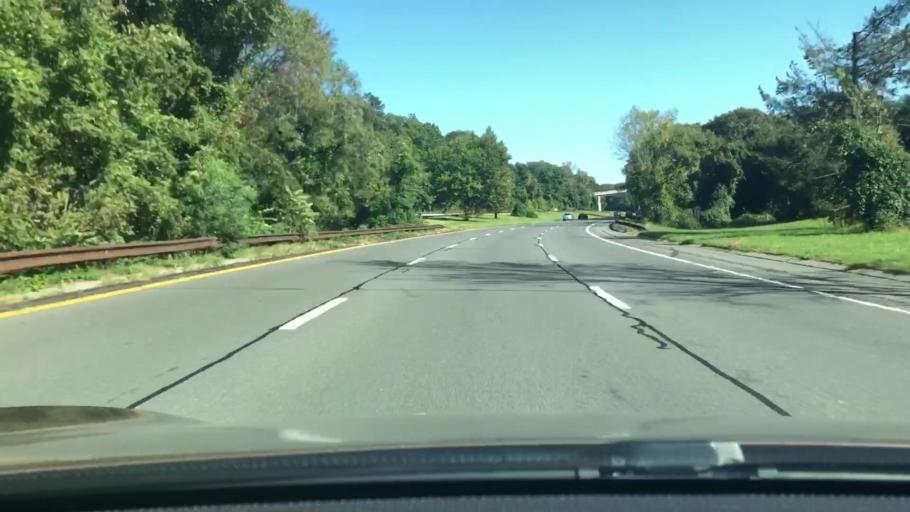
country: US
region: New York
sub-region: Westchester County
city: Ardsley
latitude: 41.0139
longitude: -73.8286
